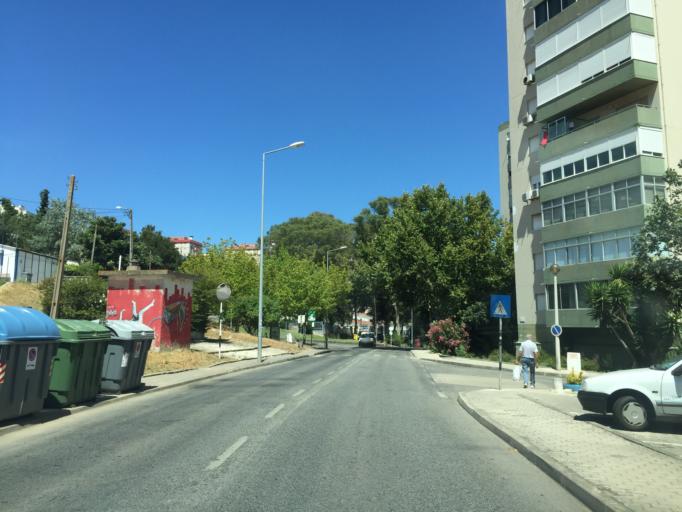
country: PT
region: Lisbon
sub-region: Odivelas
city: Povoa de Santo Adriao
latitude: 38.8111
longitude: -9.1625
